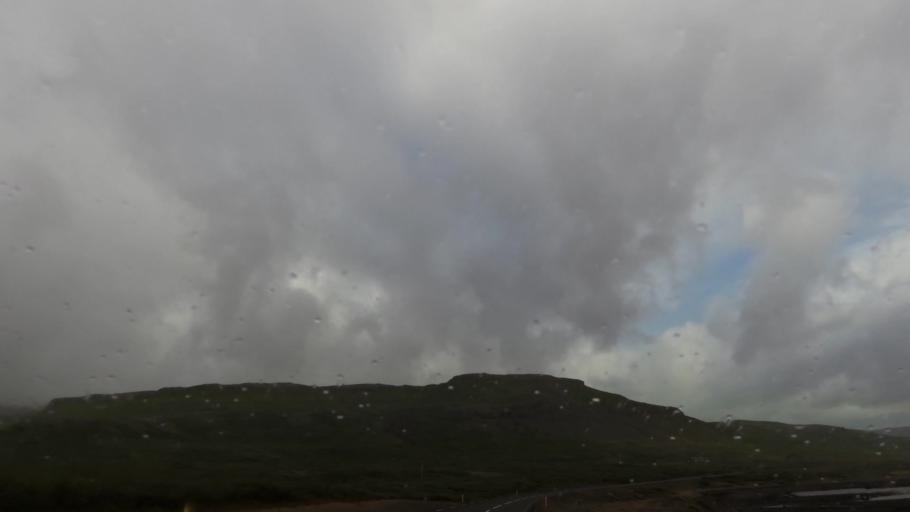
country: IS
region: Westfjords
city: Isafjoerdur
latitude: 65.5453
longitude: -23.2014
